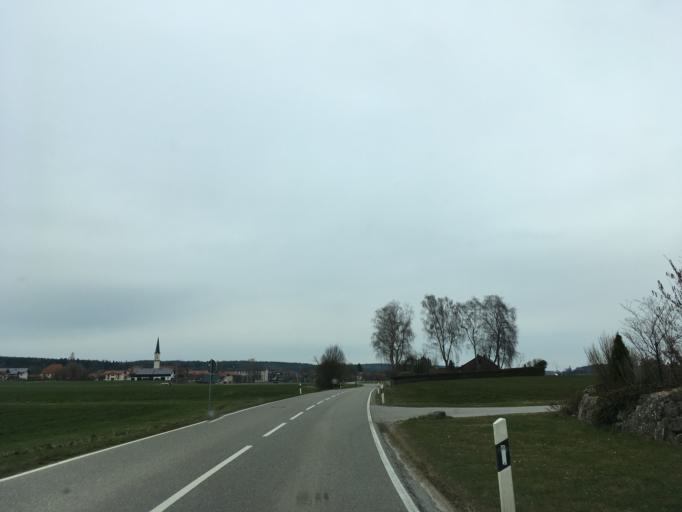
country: DE
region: Bavaria
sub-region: Upper Bavaria
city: Schnaitsee
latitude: 48.0995
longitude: 12.4077
